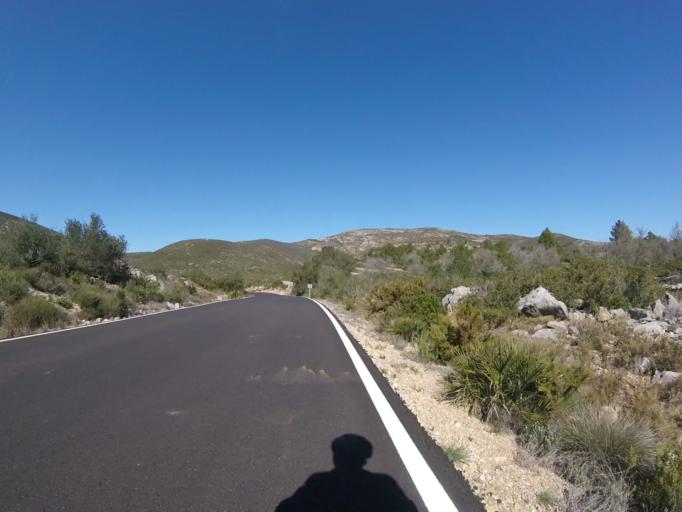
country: ES
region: Valencia
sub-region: Provincia de Castello
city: Cervera del Maestre
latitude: 40.4022
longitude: 0.2304
